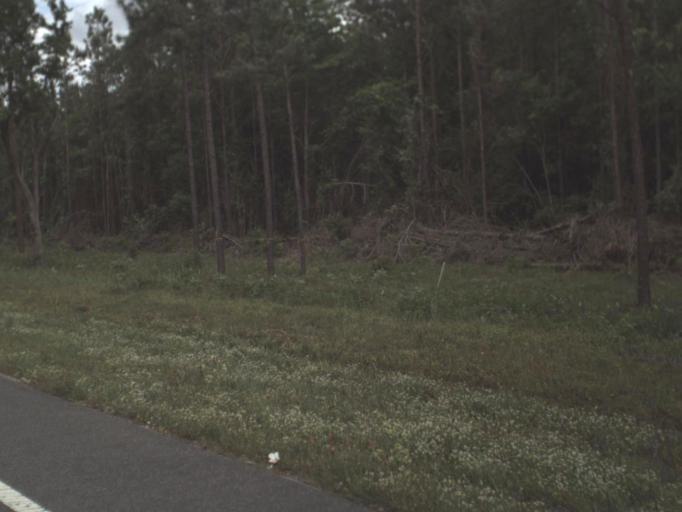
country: US
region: Florida
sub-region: Santa Rosa County
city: Point Baker
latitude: 30.7367
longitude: -87.0934
